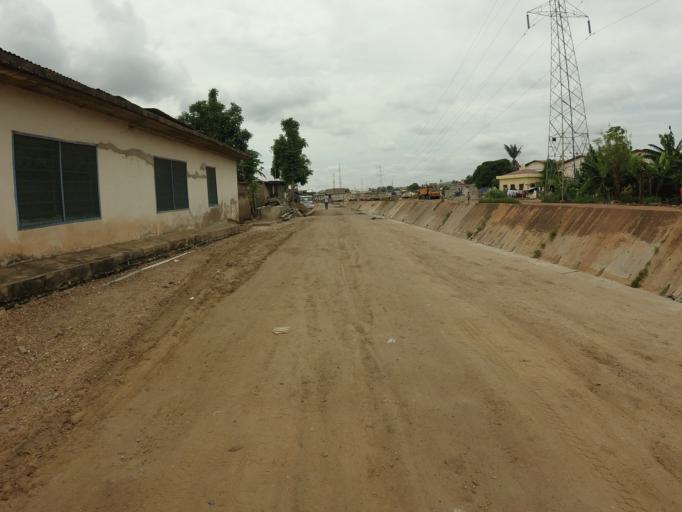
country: GH
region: Greater Accra
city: Accra
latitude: 5.5893
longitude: -0.2148
